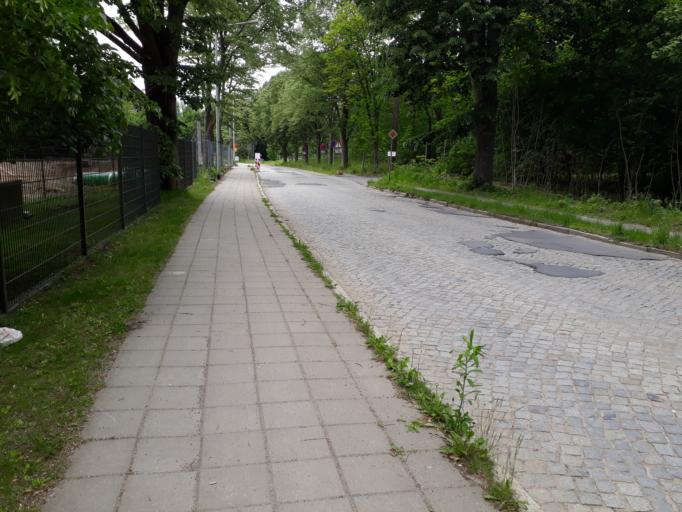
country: DE
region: Saxony
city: Albertstadt
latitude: 51.1305
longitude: 13.7881
